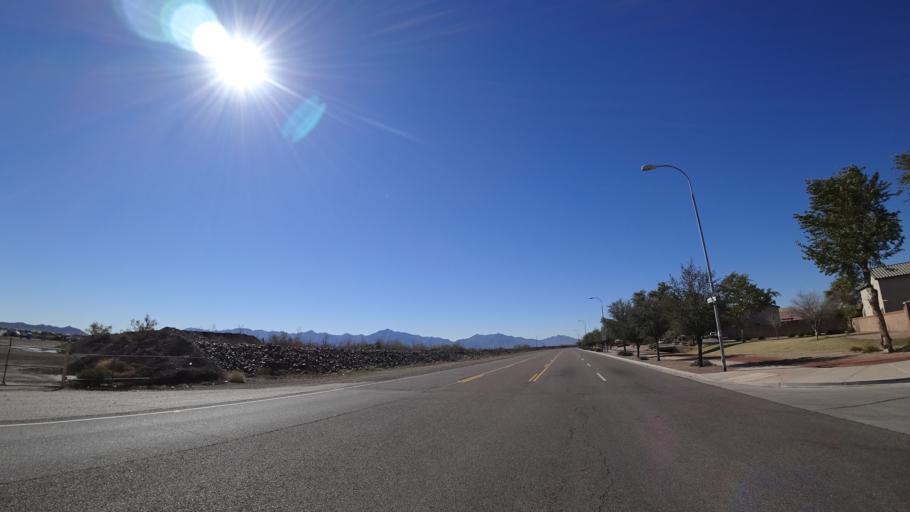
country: US
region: Arizona
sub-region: Maricopa County
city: Laveen
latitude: 33.4096
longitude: -112.1776
